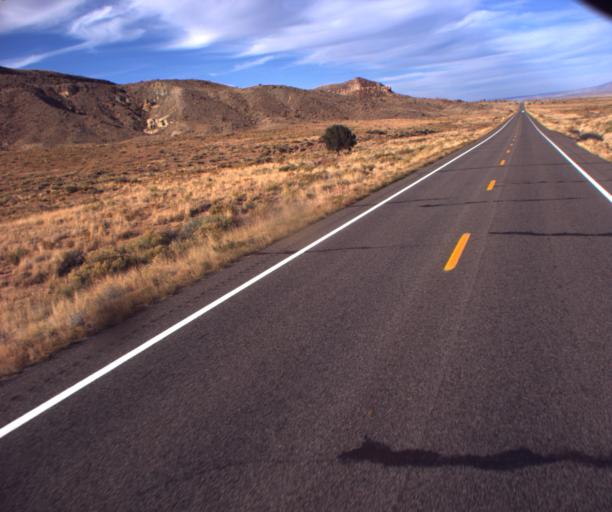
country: US
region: New Mexico
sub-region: San Juan County
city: Shiprock
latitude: 36.9321
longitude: -109.0796
